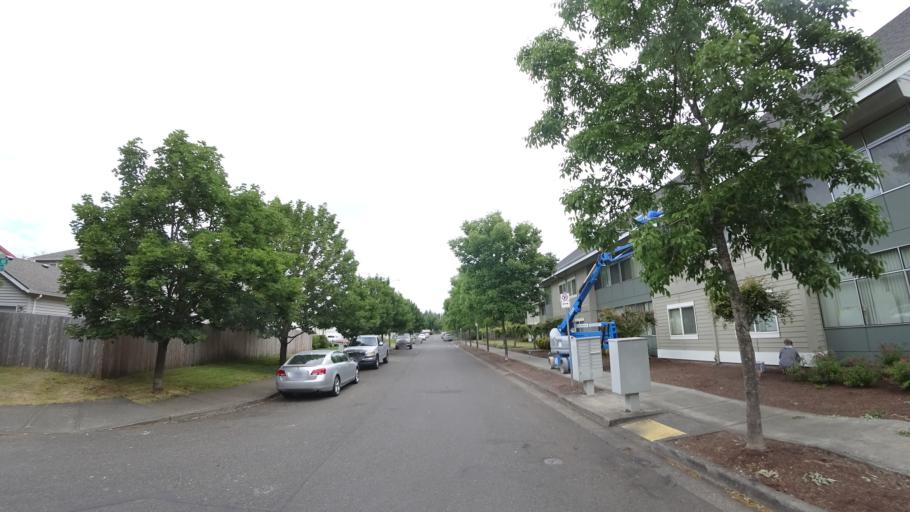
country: US
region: Oregon
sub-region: Multnomah County
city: Lents
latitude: 45.5012
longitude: -122.5325
